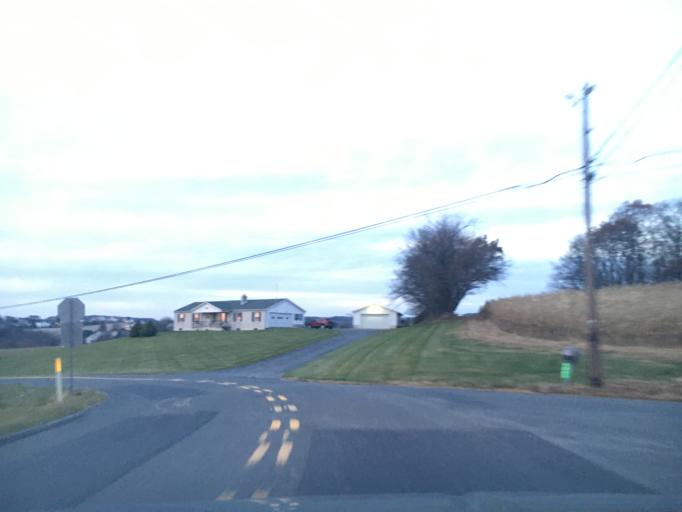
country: US
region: Pennsylvania
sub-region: Lehigh County
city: Schnecksville
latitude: 40.6952
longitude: -75.5797
